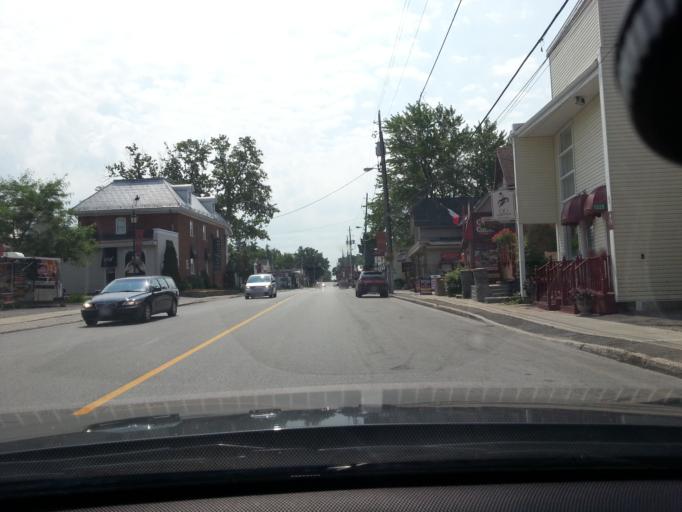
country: CA
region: Ontario
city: Bells Corners
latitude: 45.2260
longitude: -75.6855
